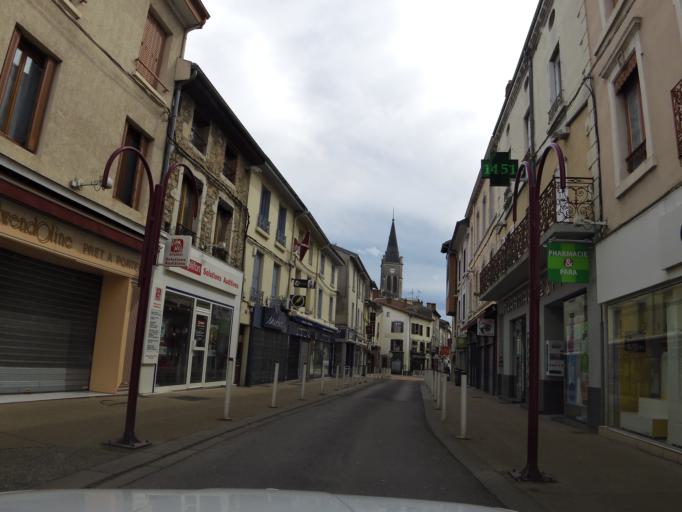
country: FR
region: Rhone-Alpes
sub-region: Departement de l'Ain
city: Amberieu-en-Bugey
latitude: 45.9591
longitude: 5.3584
